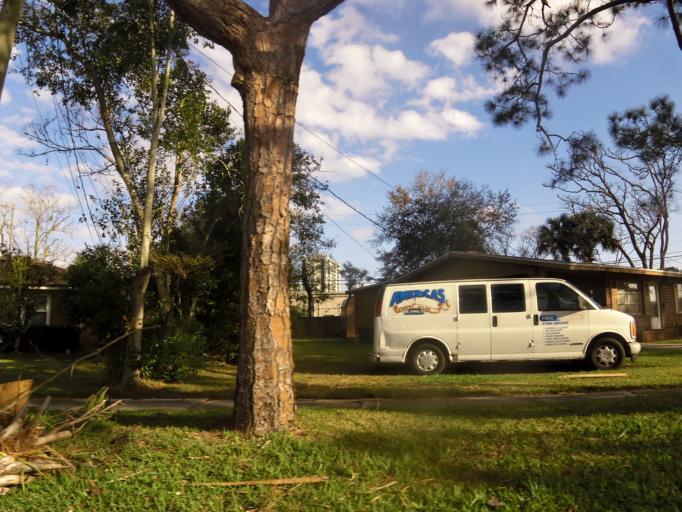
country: US
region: Florida
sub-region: Duval County
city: Jacksonville
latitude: 30.2759
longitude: -81.6071
